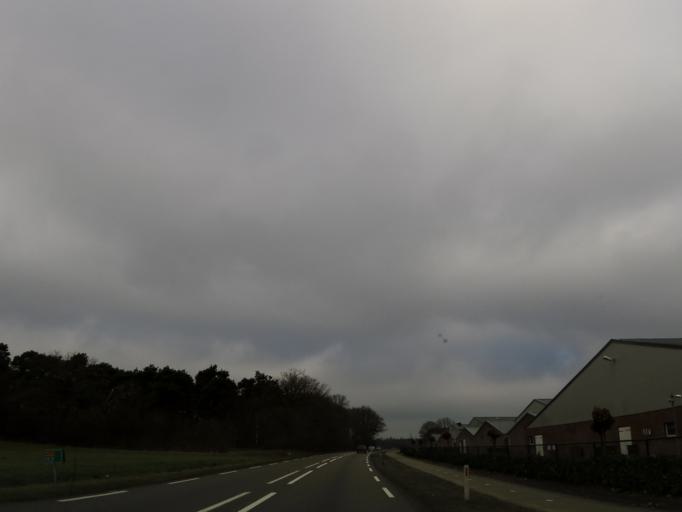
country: NL
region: Limburg
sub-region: Gemeente Peel en Maas
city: Maasbree
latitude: 51.3565
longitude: 5.9733
